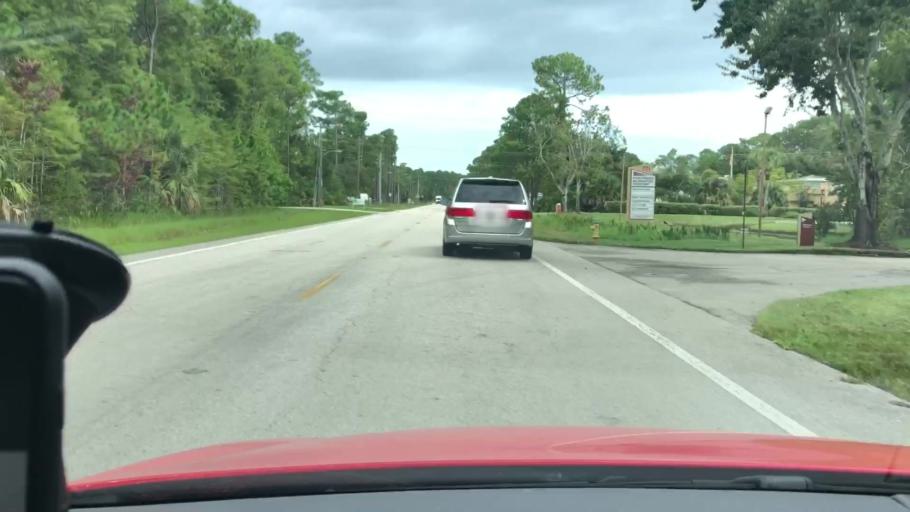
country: US
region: Florida
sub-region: Volusia County
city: Holly Hill
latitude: 29.2092
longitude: -81.0836
